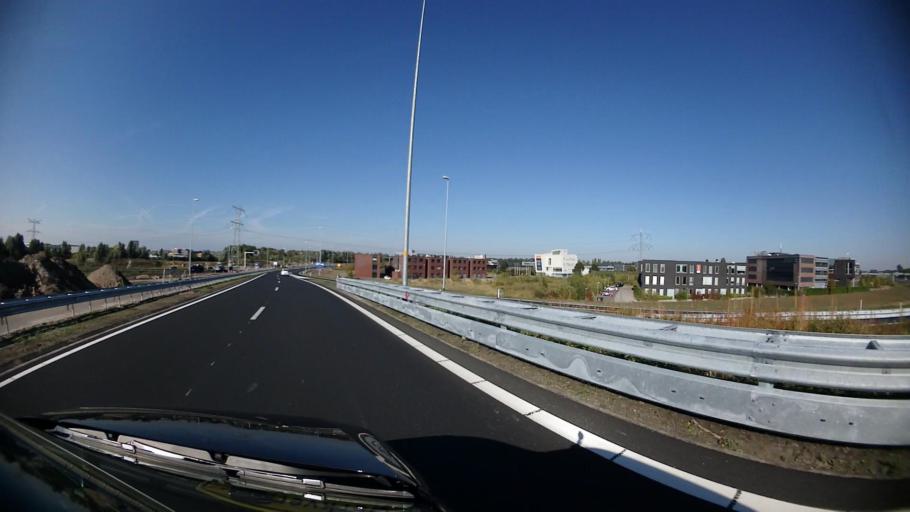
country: NL
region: Flevoland
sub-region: Gemeente Almere
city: Almere Stad
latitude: 52.3441
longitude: 5.1761
